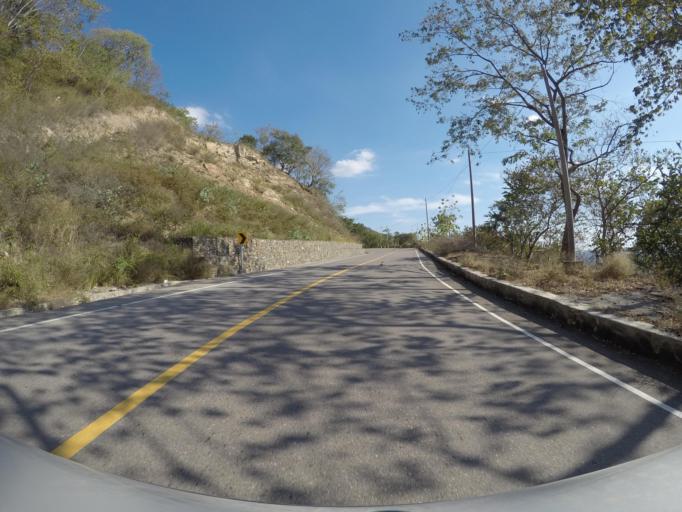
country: TL
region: Liquica
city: Maubara
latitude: -8.6438
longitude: 125.1237
